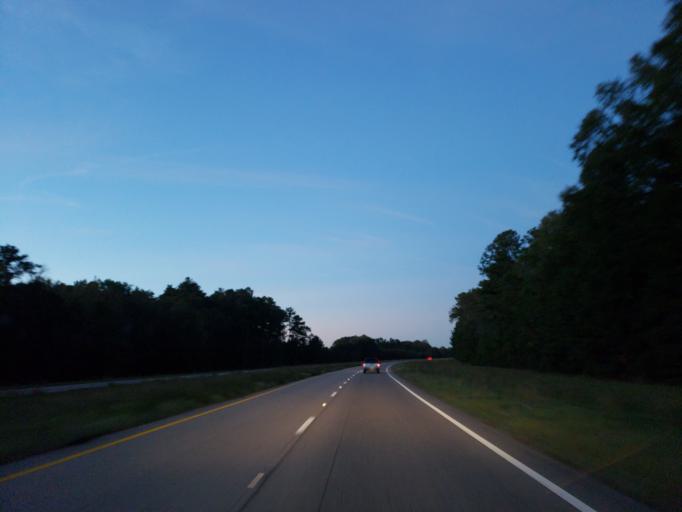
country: US
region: Mississippi
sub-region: Clarke County
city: Quitman
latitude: 31.8583
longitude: -88.7202
